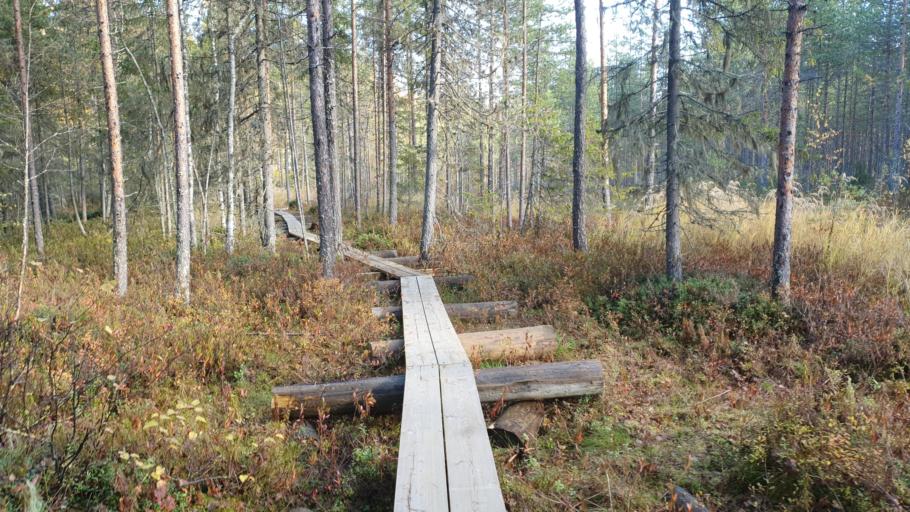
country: FI
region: Kainuu
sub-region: Kehys-Kainuu
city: Kuhmo
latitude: 64.1262
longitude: 29.4825
